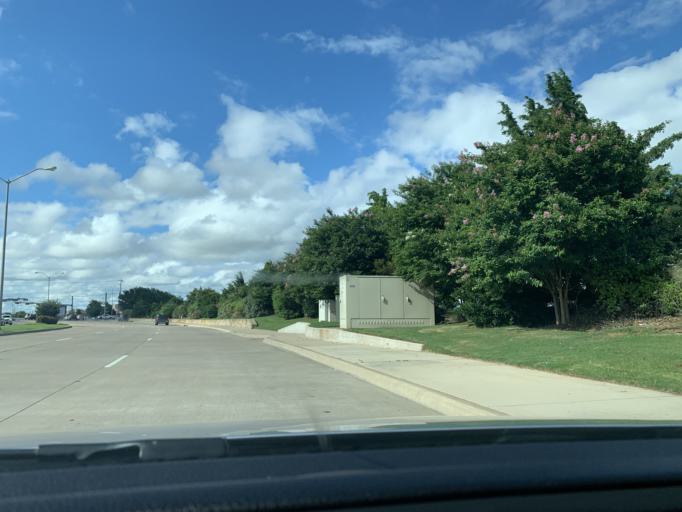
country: US
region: Texas
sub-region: Dallas County
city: Cedar Hill
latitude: 32.6459
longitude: -97.0440
